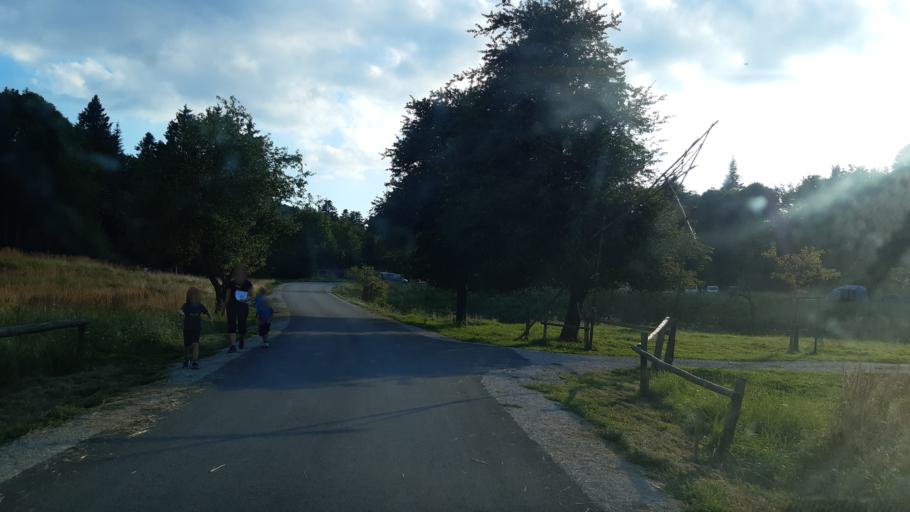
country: SI
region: Dolenjske Toplice
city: Dolenjske Toplice
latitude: 45.6758
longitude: 15.0058
